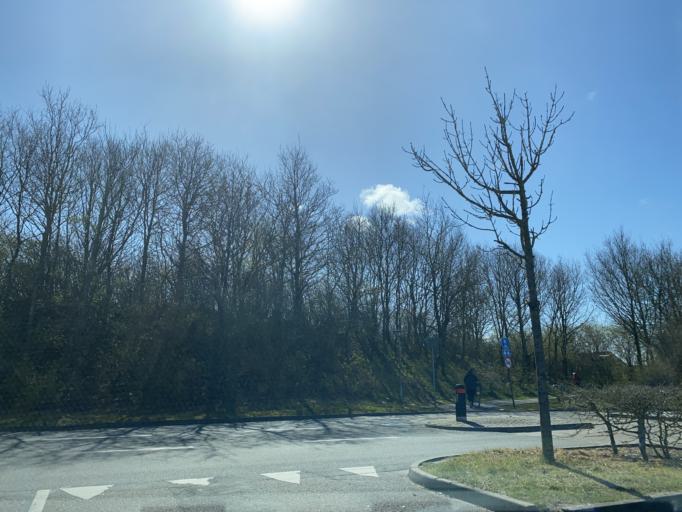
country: DK
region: Central Jutland
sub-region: Randers Kommune
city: Randers
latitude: 56.4293
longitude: 10.0666
